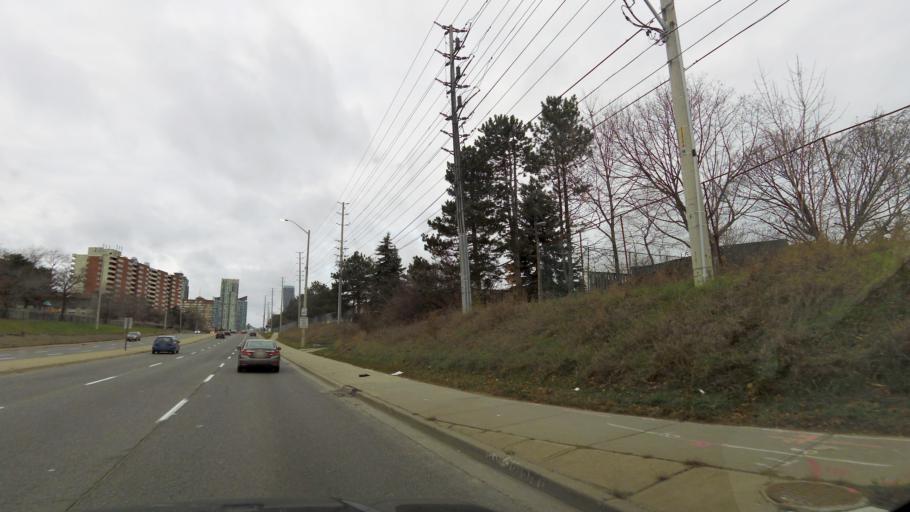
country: CA
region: Ontario
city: Mississauga
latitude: 43.5847
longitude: -79.6224
